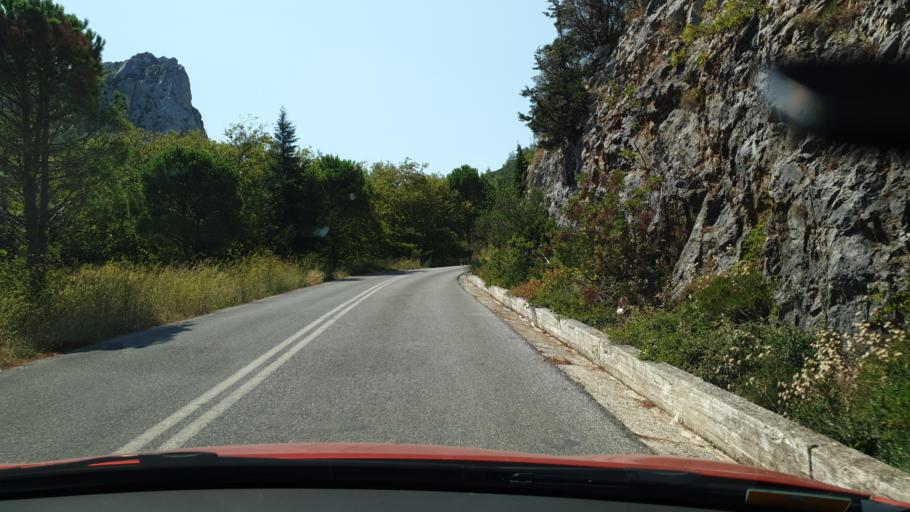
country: GR
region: Central Greece
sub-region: Nomos Evvoias
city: Kymi
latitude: 38.6292
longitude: 24.1013
